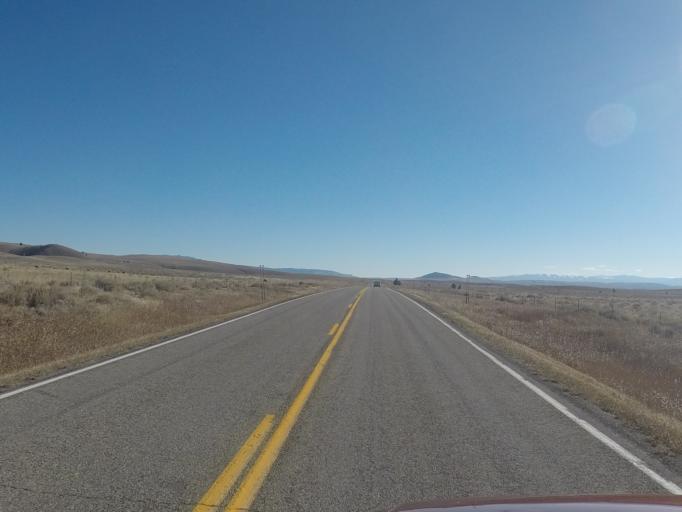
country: US
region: Montana
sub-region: Meagher County
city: White Sulphur Springs
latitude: 46.3527
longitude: -111.0545
